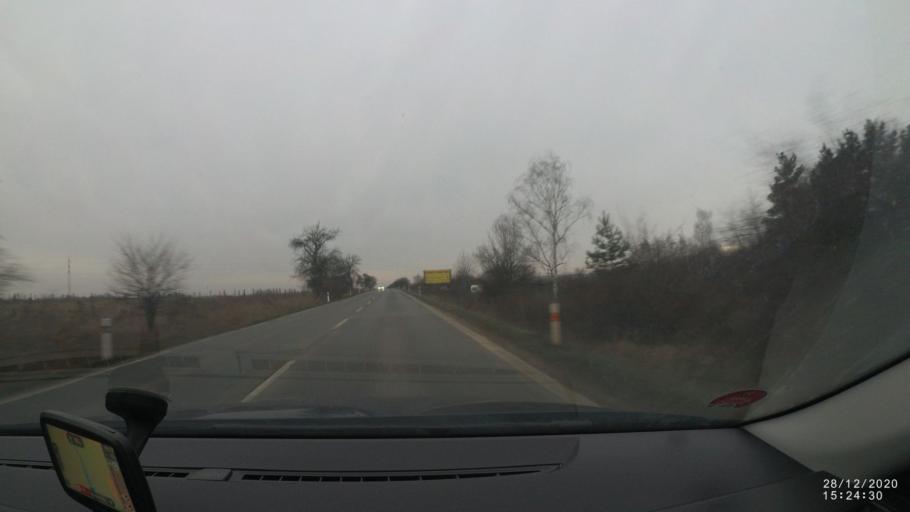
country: CZ
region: Praha
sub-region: Praha 20
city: Horni Pocernice
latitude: 50.0796
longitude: 14.6392
